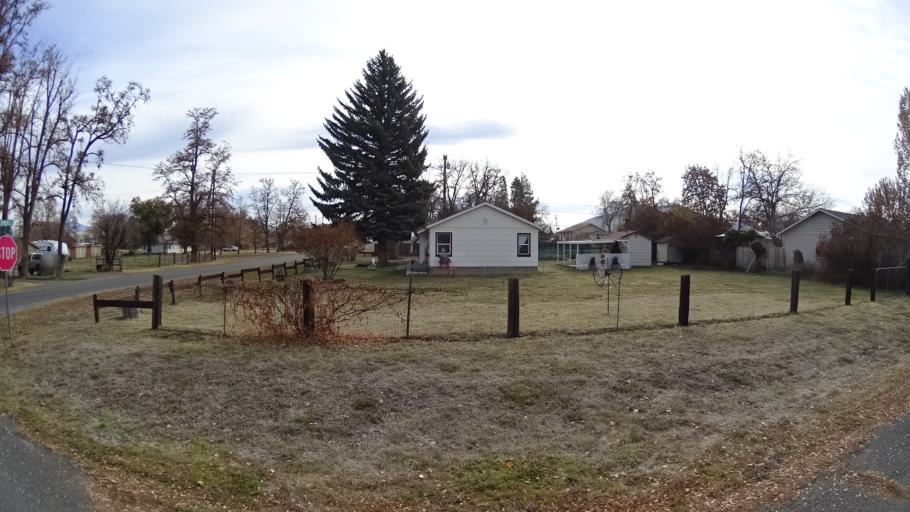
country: US
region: California
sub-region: Siskiyou County
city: Montague
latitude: 41.7314
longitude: -122.5286
